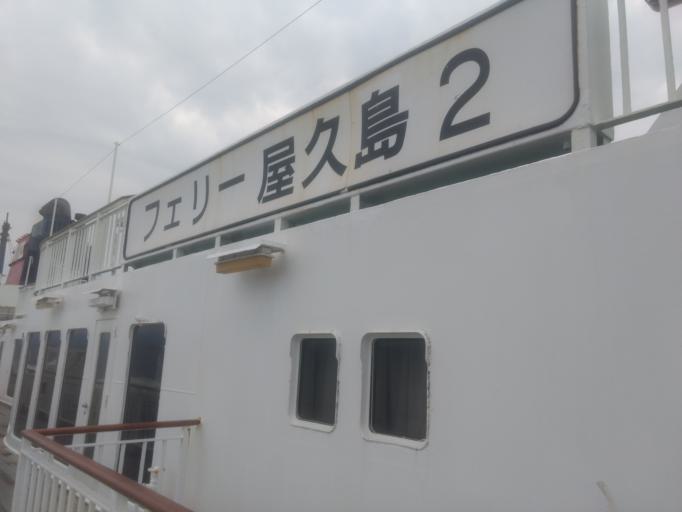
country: JP
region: Kagoshima
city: Tarumizu
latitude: 31.4143
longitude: 130.6520
